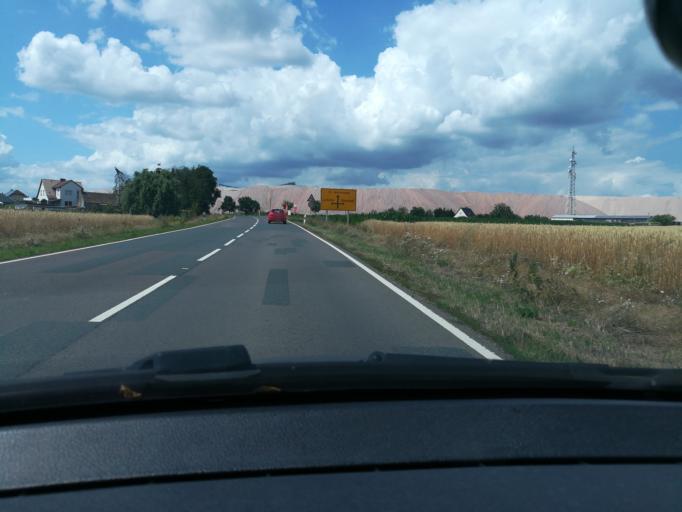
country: DE
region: Saxony-Anhalt
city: Zielitz
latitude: 52.3010
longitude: 11.7067
